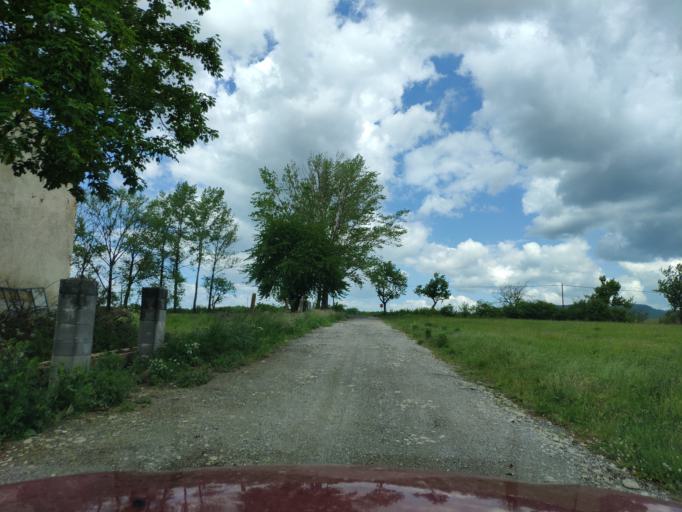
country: SK
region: Kosicky
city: Kosice
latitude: 48.8453
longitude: 21.3252
